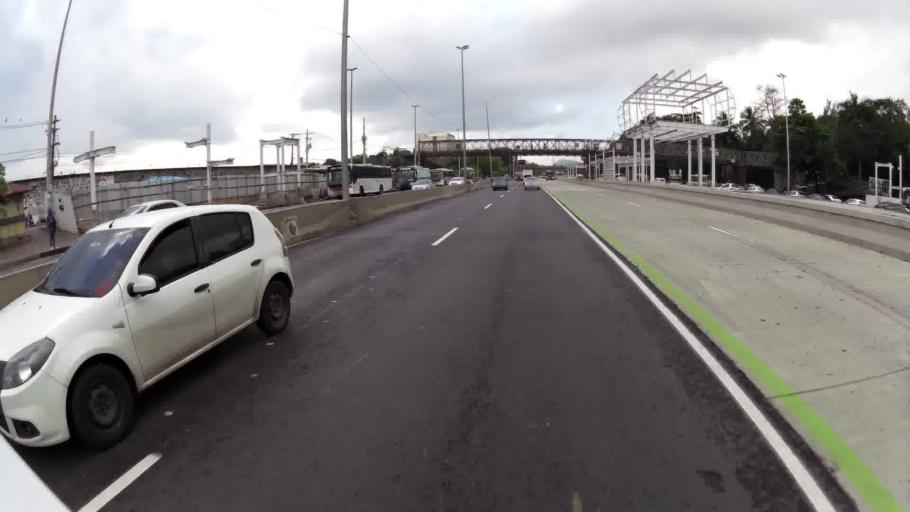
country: BR
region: Rio de Janeiro
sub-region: Rio De Janeiro
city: Rio de Janeiro
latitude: -22.8748
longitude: -43.2433
